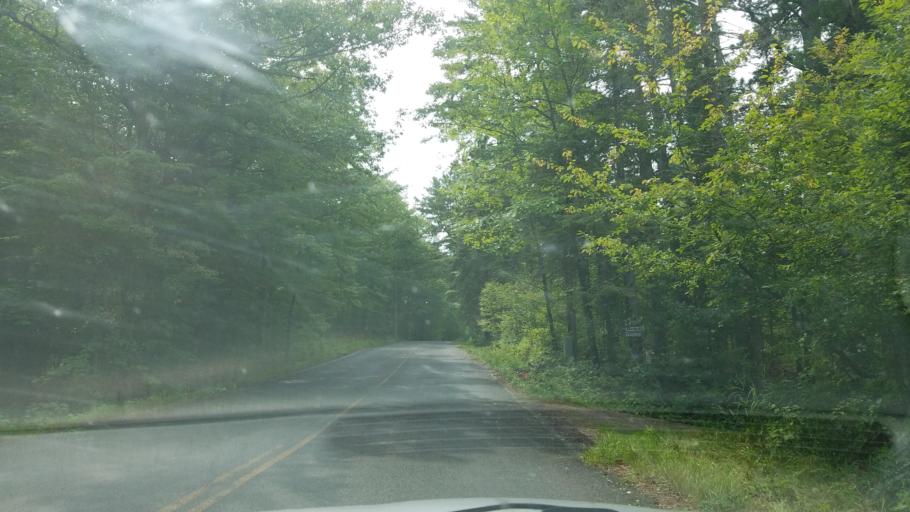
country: US
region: Wisconsin
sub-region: Bayfield County
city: Washburn
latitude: 46.7682
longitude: -90.7806
